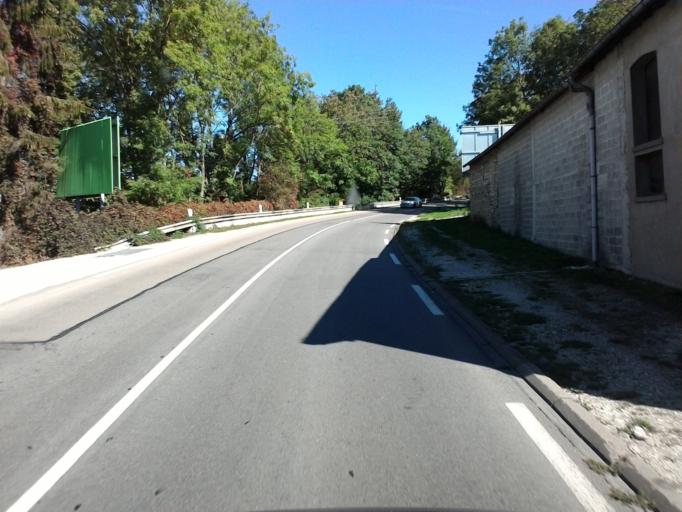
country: FR
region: Champagne-Ardenne
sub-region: Departement de la Haute-Marne
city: Chaumont
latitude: 48.1175
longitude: 5.1551
